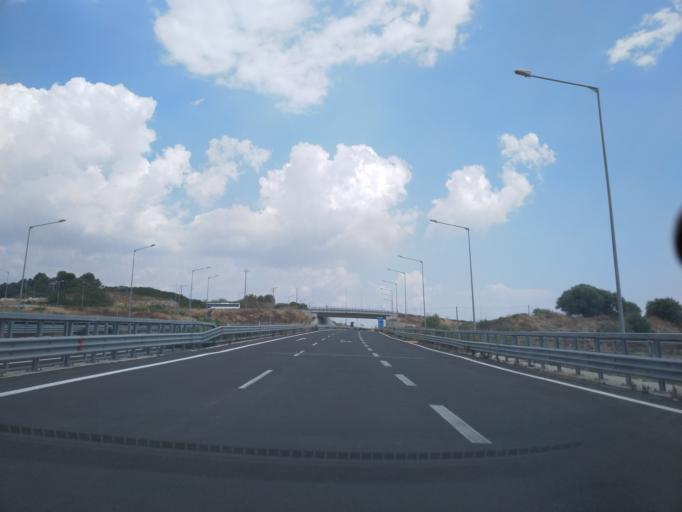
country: IT
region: Sicily
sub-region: Agrigento
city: Castrofilippo
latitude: 37.3845
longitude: 13.7673
